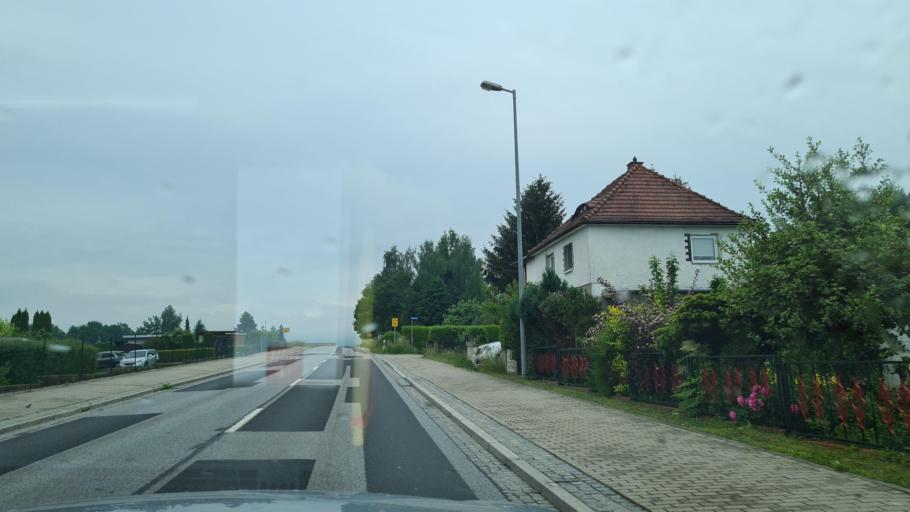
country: DE
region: Saxony
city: Grosspostwitz
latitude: 51.1108
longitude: 14.4460
